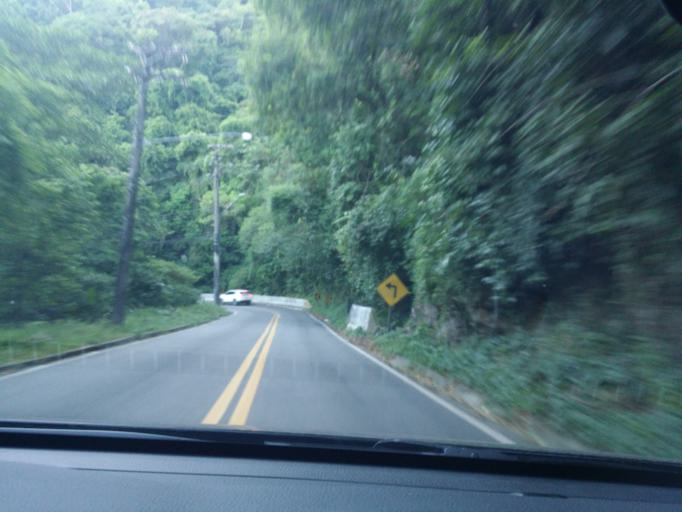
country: BR
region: Sao Paulo
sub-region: Sao Sebastiao
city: Sao Sebastiao
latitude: -23.7841
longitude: -45.5982
